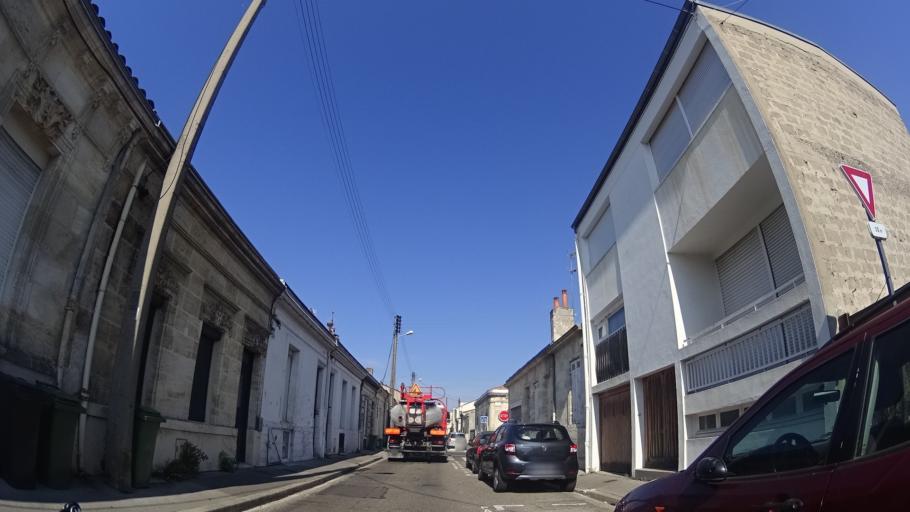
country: FR
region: Aquitaine
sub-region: Departement de la Gironde
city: Talence
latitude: 44.8179
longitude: -0.5813
